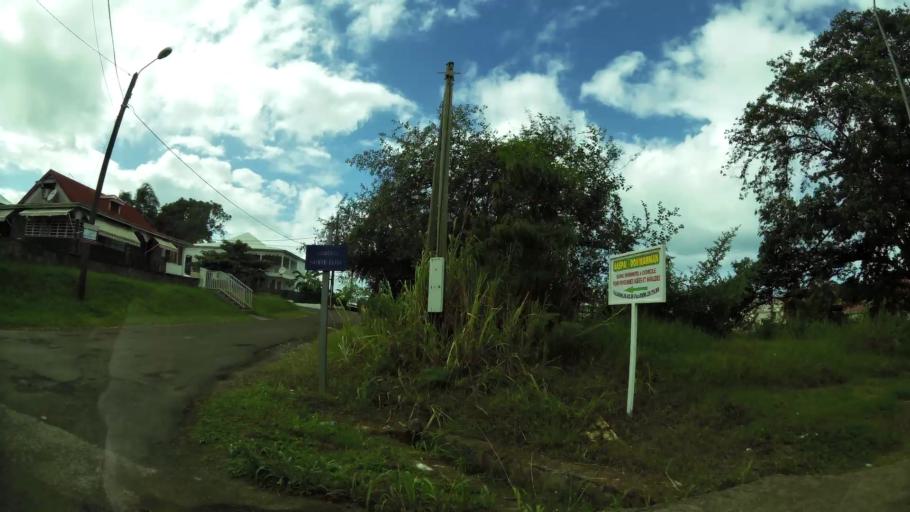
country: GP
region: Guadeloupe
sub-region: Guadeloupe
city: Sainte-Rose
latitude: 16.3274
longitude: -61.7006
